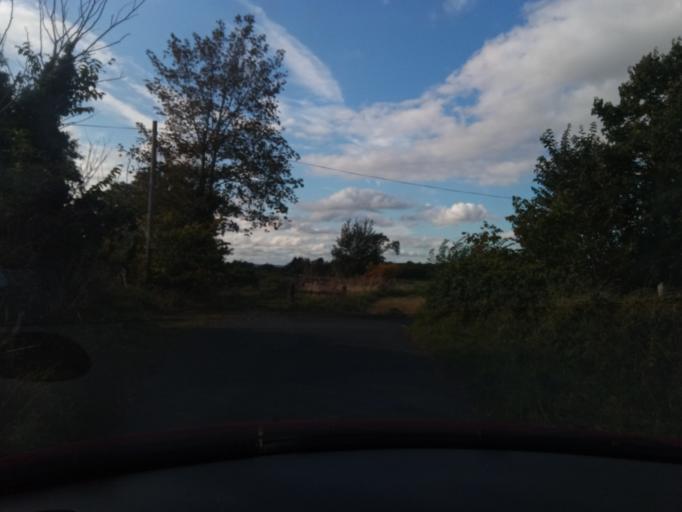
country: GB
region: Scotland
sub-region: The Scottish Borders
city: Kelso
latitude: 55.5215
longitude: -2.3452
